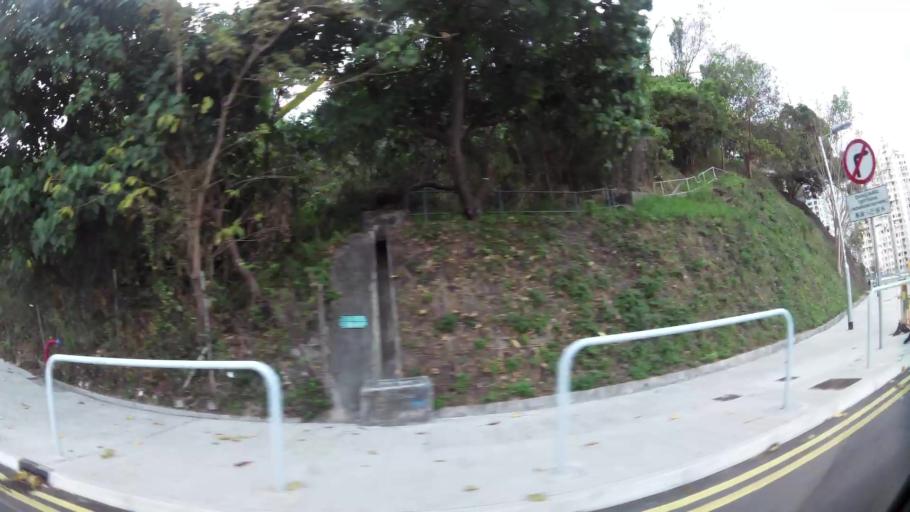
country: HK
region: Kowloon City
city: Kowloon
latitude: 22.3091
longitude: 114.1815
